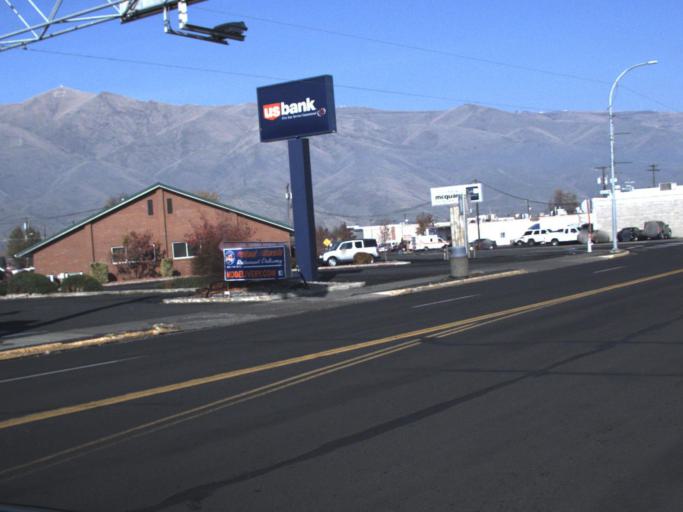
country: US
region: Washington
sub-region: Asotin County
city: Clarkston
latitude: 46.4172
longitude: -117.0443
